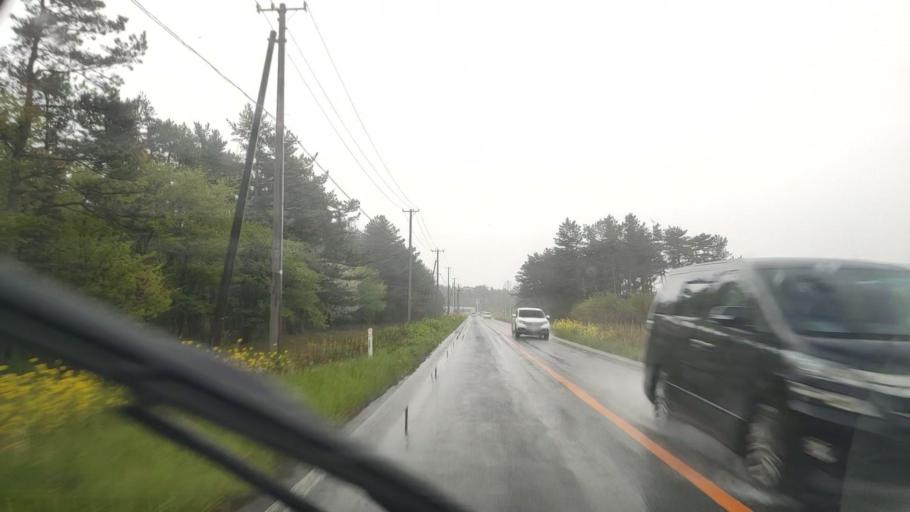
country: JP
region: Akita
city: Tenno
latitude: 40.0150
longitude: 139.9528
